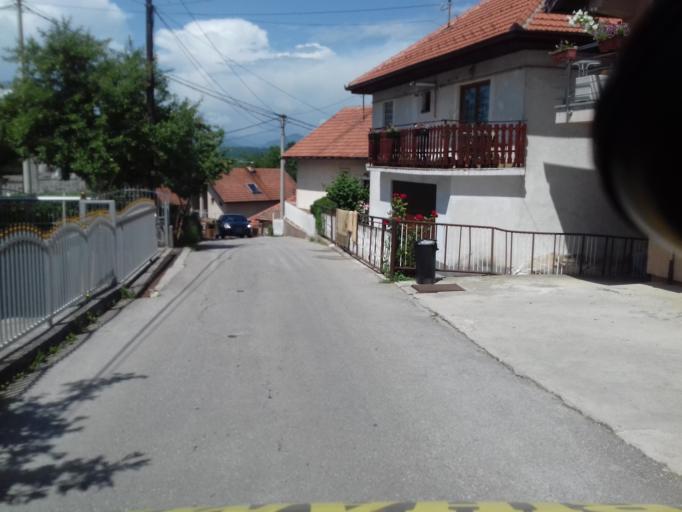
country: BA
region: Federation of Bosnia and Herzegovina
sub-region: Kanton Sarajevo
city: Sarajevo
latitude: 43.8625
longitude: 18.3195
